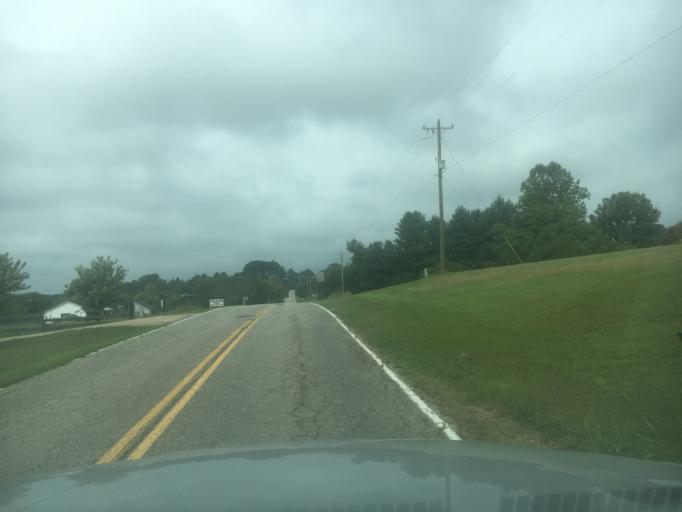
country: US
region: South Carolina
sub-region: Spartanburg County
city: Landrum
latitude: 35.1661
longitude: -82.0771
